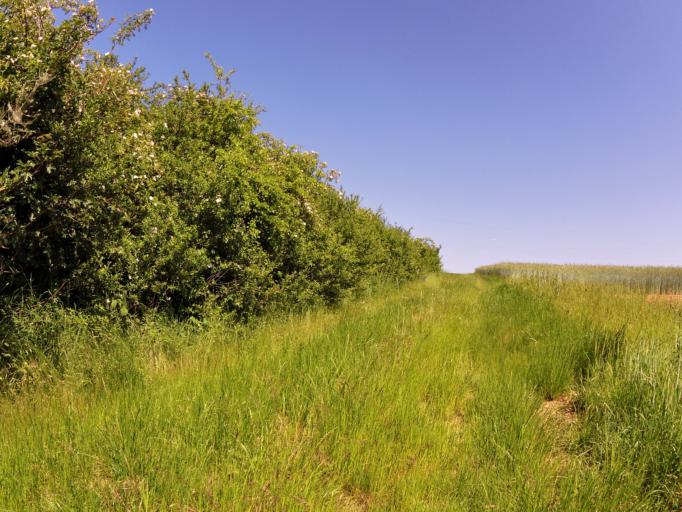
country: DE
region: Bavaria
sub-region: Regierungsbezirk Unterfranken
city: Kleinrinderfeld
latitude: 49.7107
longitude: 9.8448
